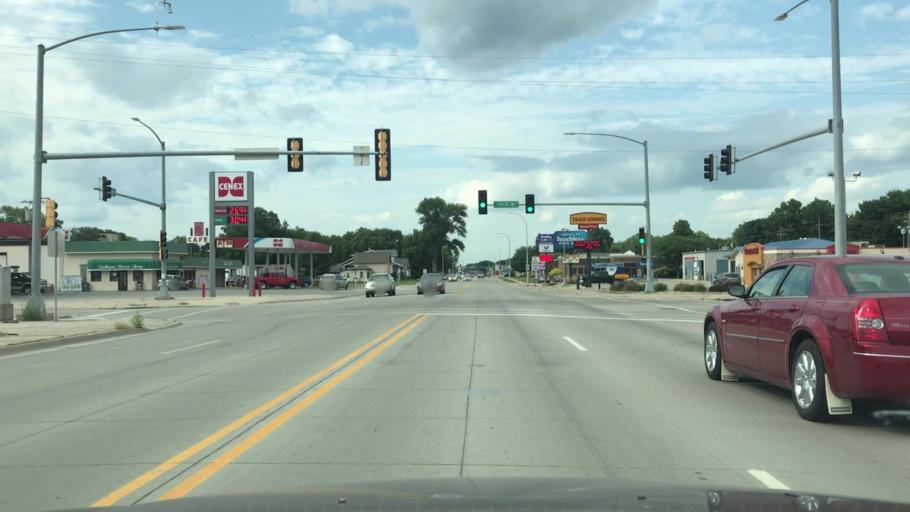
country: US
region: Iowa
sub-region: Plymouth County
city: Le Mars
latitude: 42.7878
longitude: -96.1738
